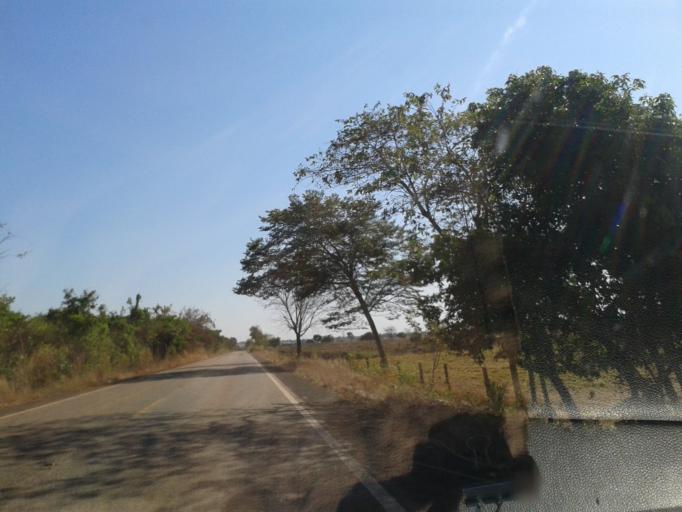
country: BR
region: Goias
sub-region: Mozarlandia
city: Mozarlandia
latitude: -14.6297
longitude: -50.5190
